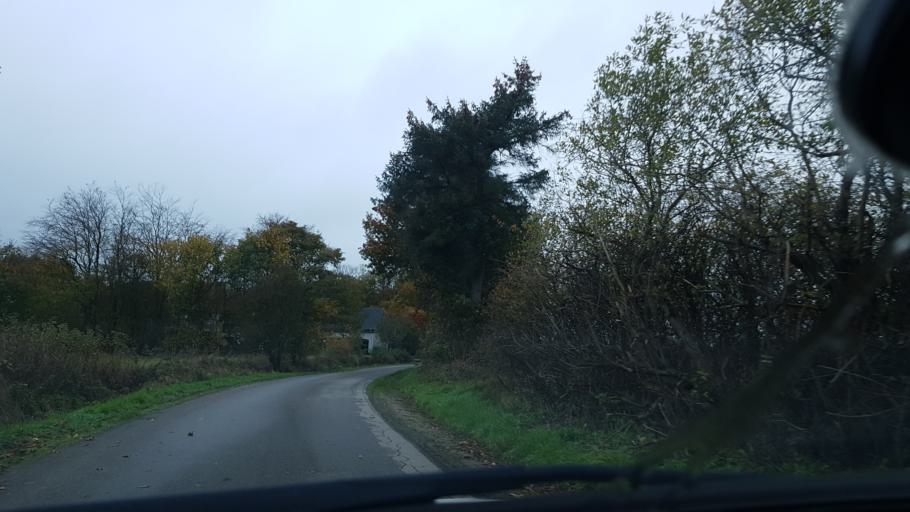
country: DK
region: South Denmark
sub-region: Esbjerg Kommune
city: Ribe
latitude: 55.2806
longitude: 8.8387
